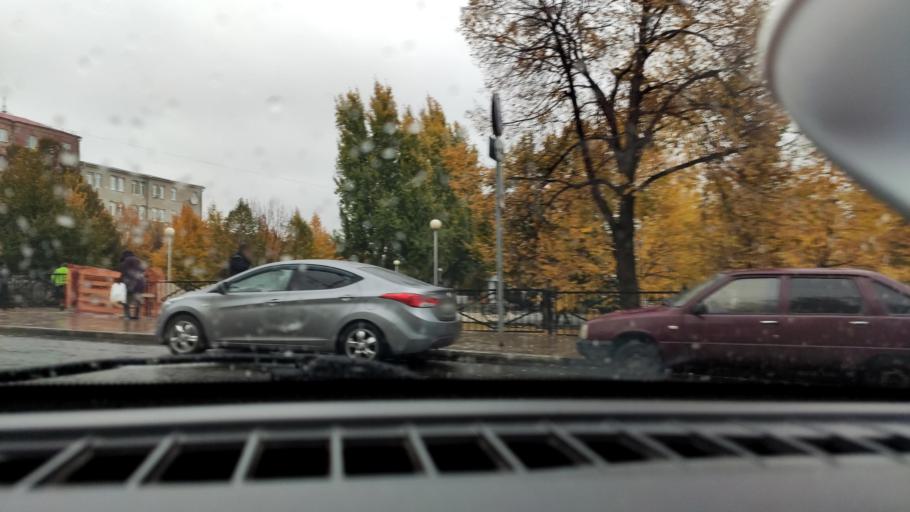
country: RU
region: Samara
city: Samara
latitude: 53.1863
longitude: 50.0983
